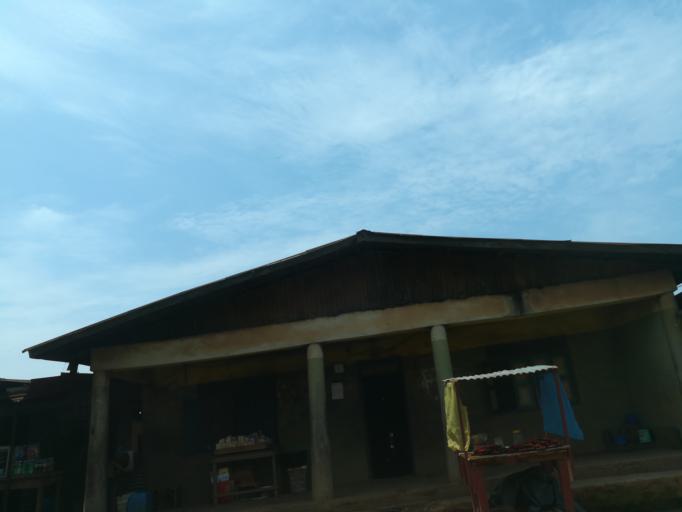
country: NG
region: Lagos
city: Ikorodu
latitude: 6.6230
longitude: 3.4950
